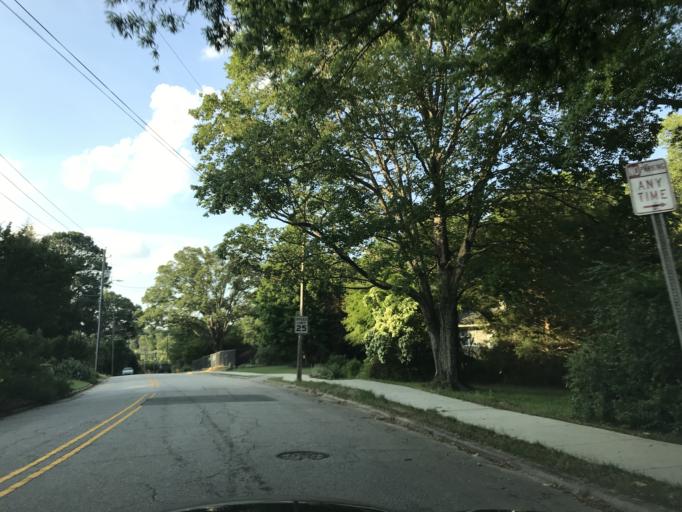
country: US
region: North Carolina
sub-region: Wake County
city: West Raleigh
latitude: 35.7939
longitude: -78.6560
